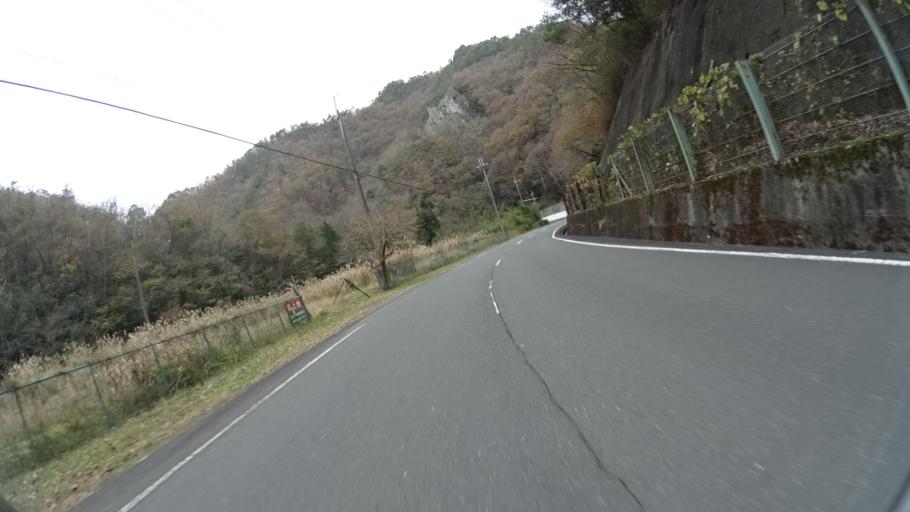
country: JP
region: Hyogo
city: Sasayama
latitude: 35.1662
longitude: 135.3151
